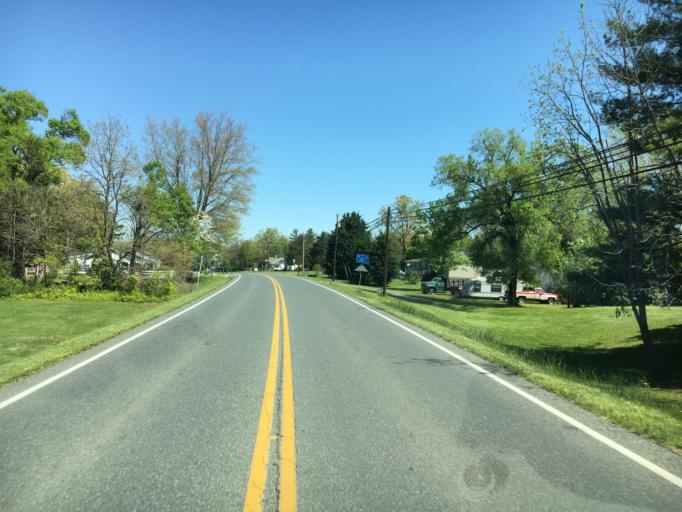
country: US
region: Virginia
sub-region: Augusta County
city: Crimora
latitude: 38.1476
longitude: -78.8408
